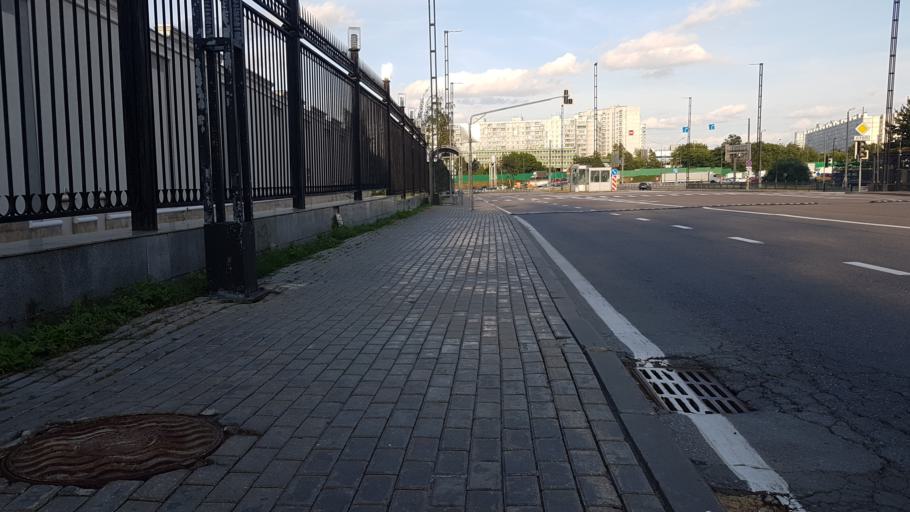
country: RU
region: Moscow
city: Strogino
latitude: 55.8152
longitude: 37.3866
